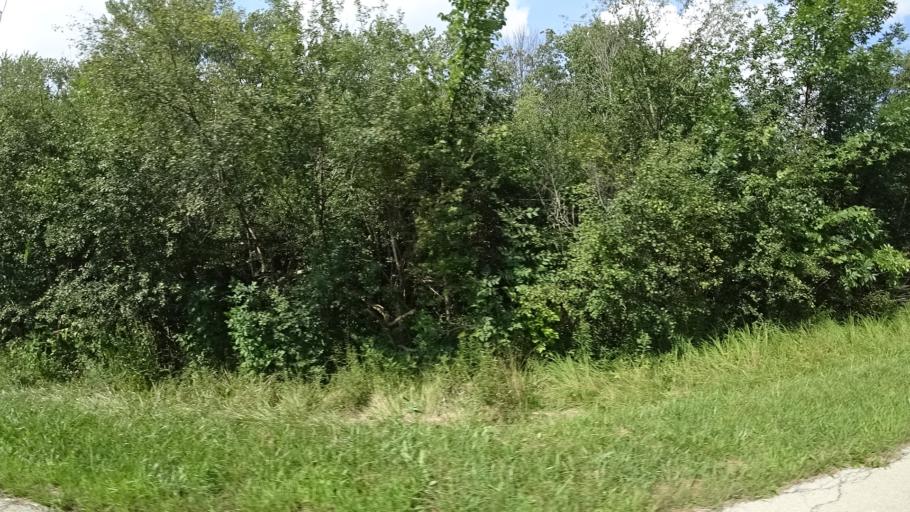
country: US
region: Illinois
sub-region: Will County
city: Goodings Grove
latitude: 41.6516
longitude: -87.8944
